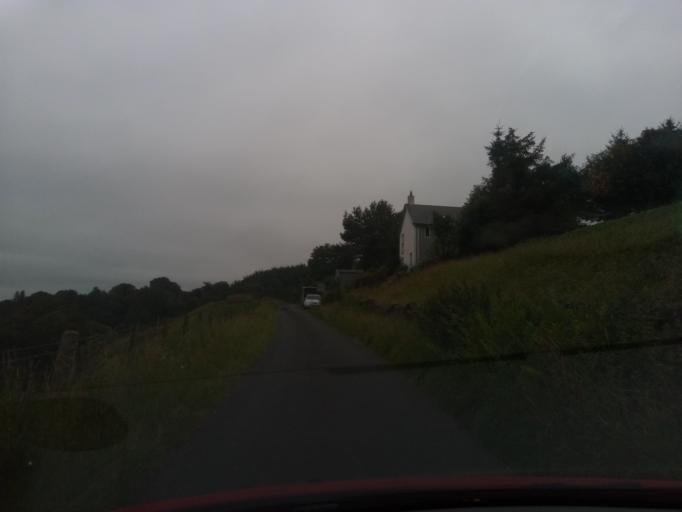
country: GB
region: Scotland
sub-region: Fife
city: Pathhead
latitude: 55.7448
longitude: -2.9234
